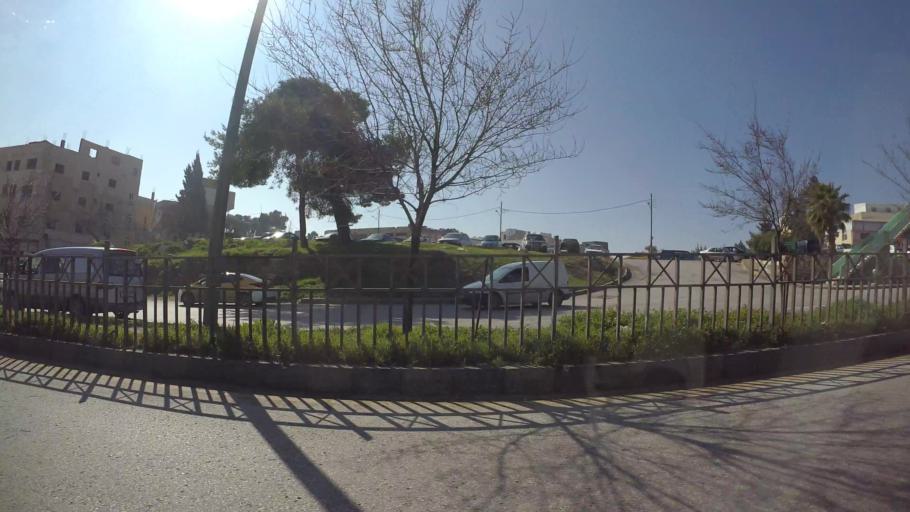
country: JO
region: Amman
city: Al Bunayyat ash Shamaliyah
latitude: 31.9104
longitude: 35.8924
